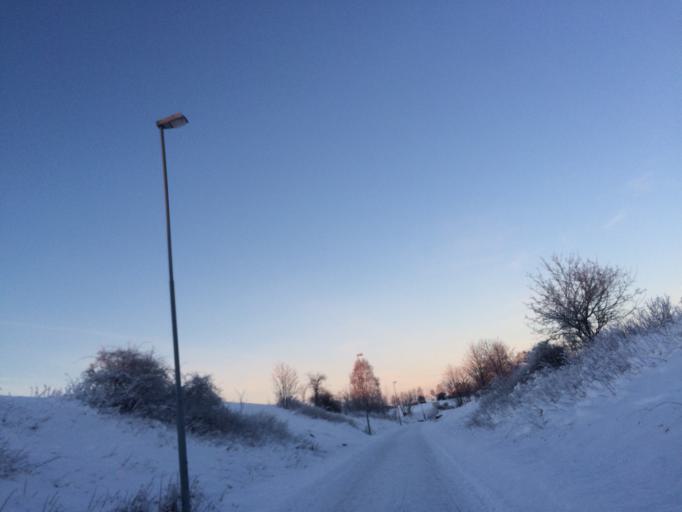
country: NO
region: Akershus
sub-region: Ski
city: Ski
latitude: 59.7008
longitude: 10.8322
